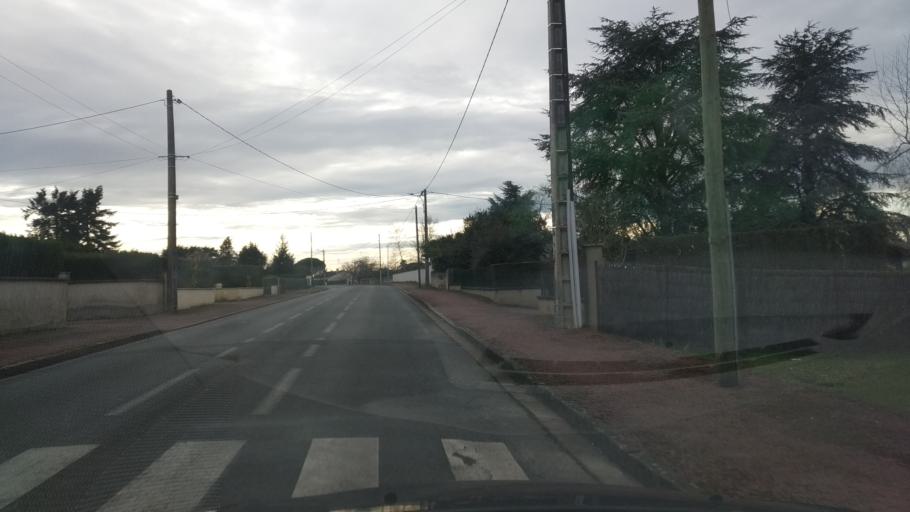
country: FR
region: Poitou-Charentes
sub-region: Departement de la Vienne
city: Dissay
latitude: 46.6904
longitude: 0.4178
